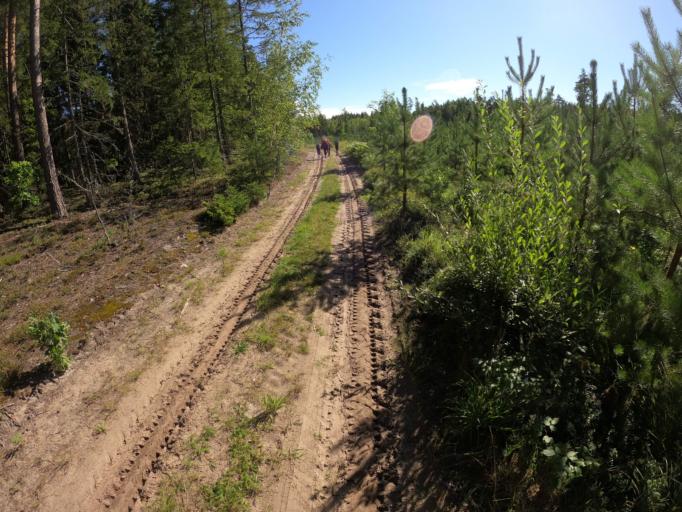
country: LV
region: Talsu Rajons
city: Stende
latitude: 57.0701
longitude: 22.3466
